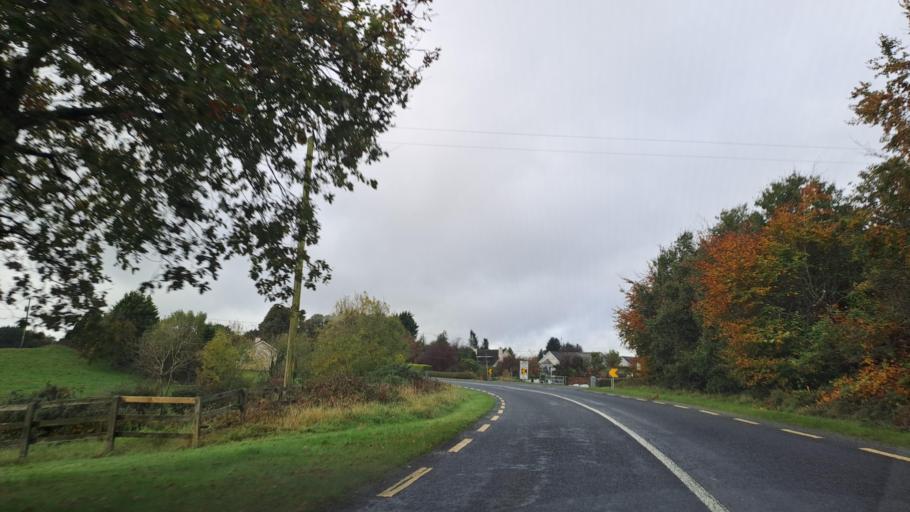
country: IE
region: Ulster
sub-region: An Cabhan
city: Bailieborough
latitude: 53.9060
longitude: -6.9868
